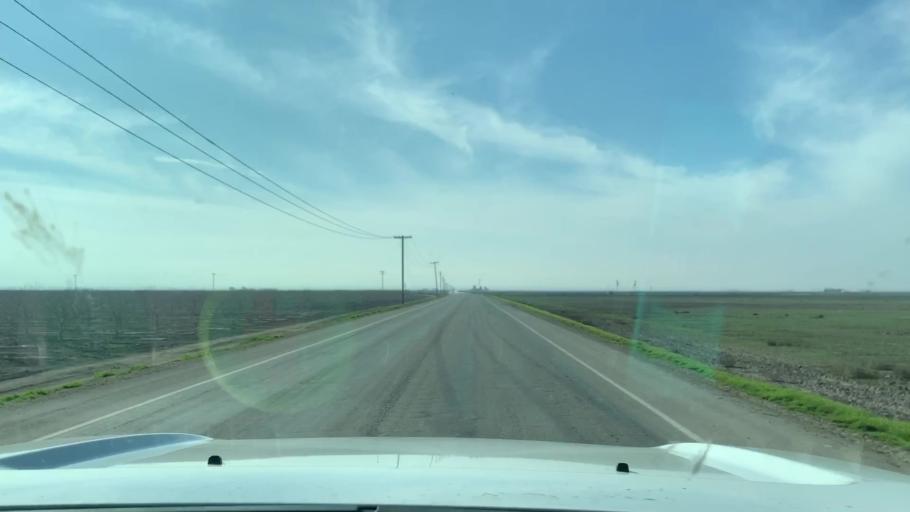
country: US
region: California
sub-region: Kern County
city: Buttonwillow
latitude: 35.4424
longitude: -119.4979
